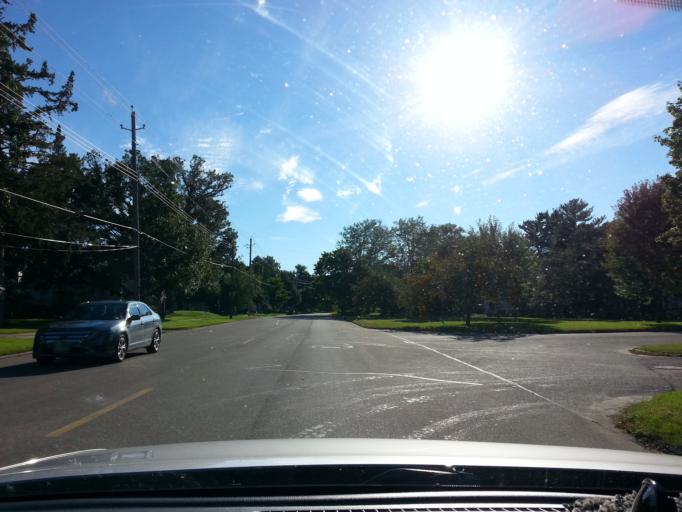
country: US
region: Minnesota
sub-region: Olmsted County
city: Rochester
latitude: 44.0112
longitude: -92.4720
